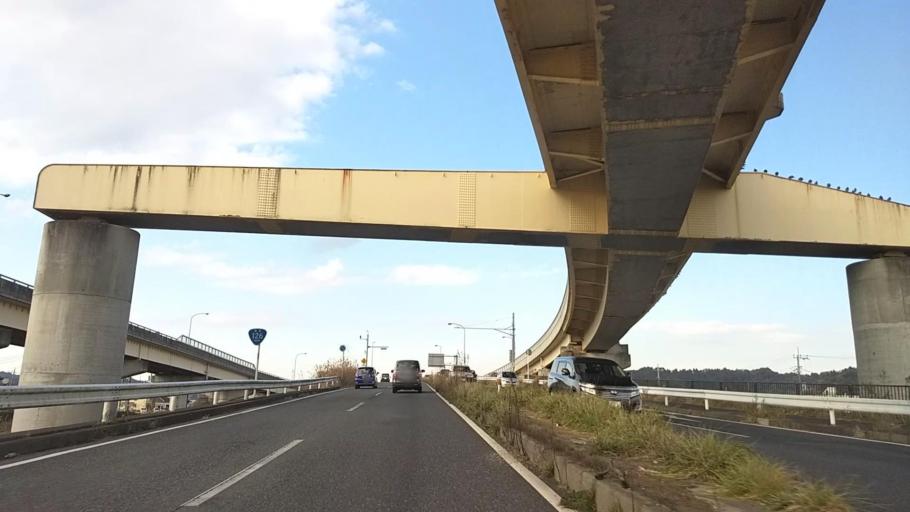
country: JP
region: Chiba
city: Togane
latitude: 35.5509
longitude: 140.3496
